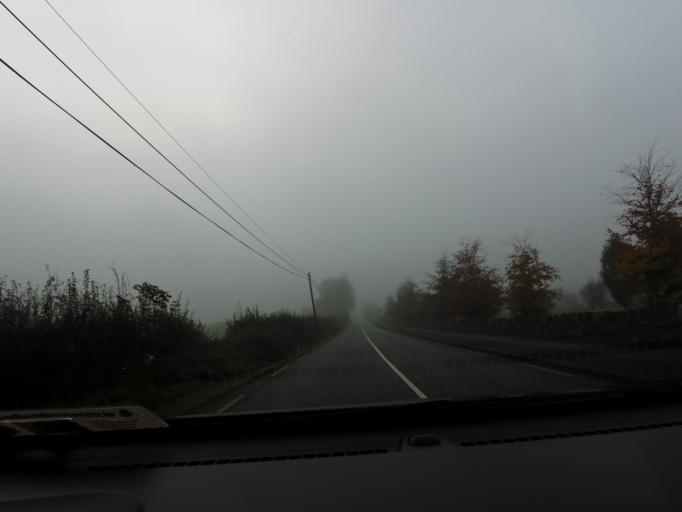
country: IE
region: Leinster
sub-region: An Iarmhi
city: Moate
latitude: 53.3777
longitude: -7.7985
